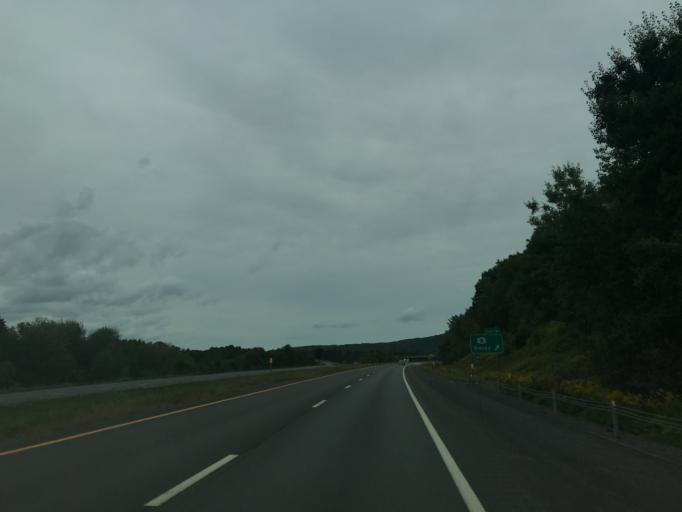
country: US
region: New York
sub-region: Delaware County
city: Sidney
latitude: 42.2930
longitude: -75.4153
